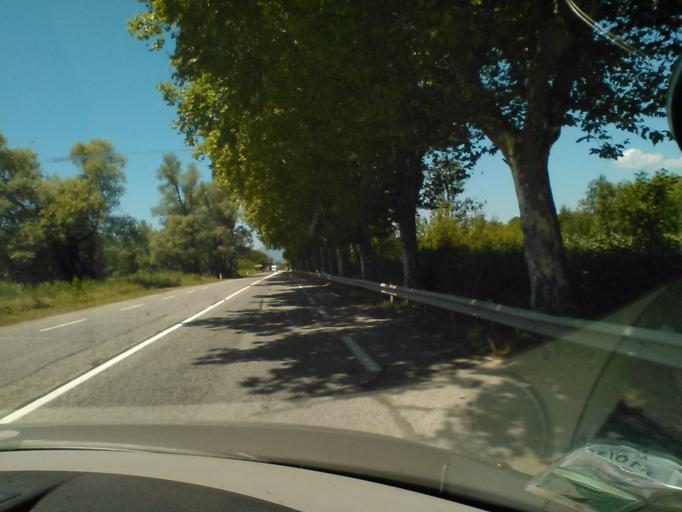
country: FR
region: Rhone-Alpes
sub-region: Departement de la Savoie
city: Les Marches
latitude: 45.5089
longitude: 6.0177
